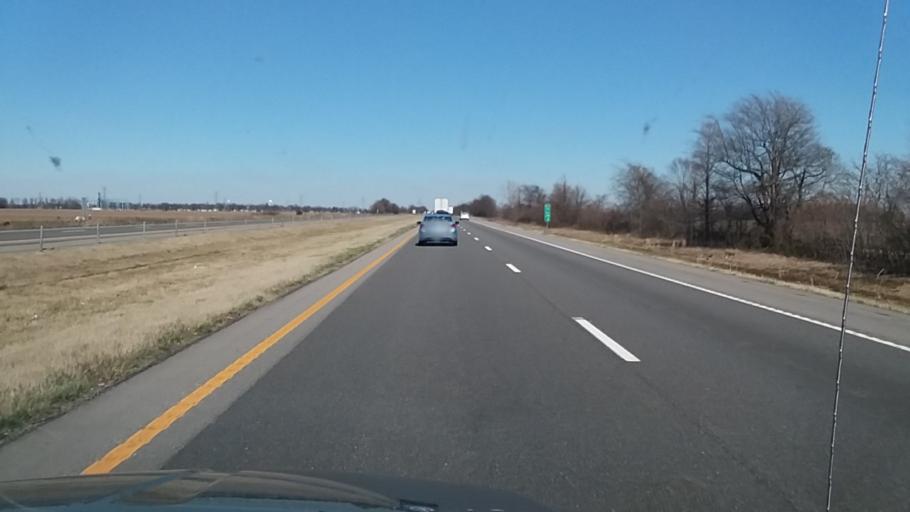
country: US
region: Missouri
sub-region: New Madrid County
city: Lilbourn
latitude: 36.4927
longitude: -89.6230
